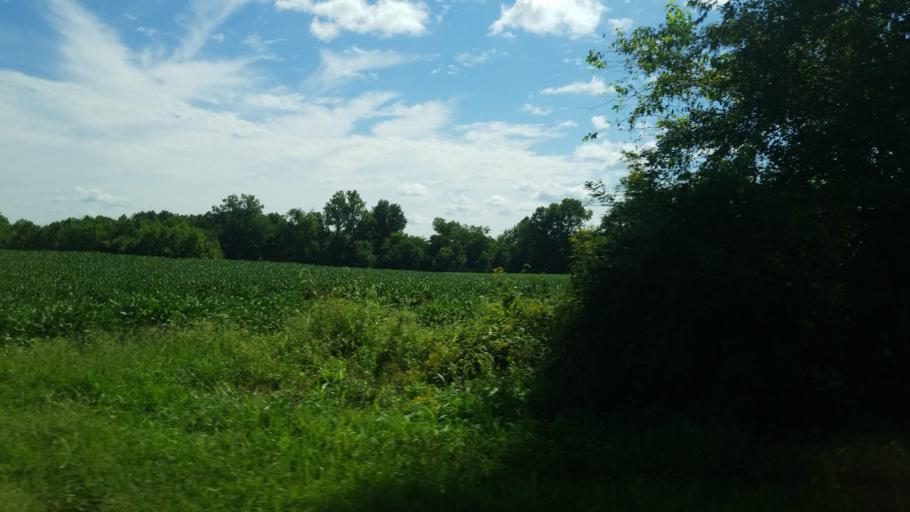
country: US
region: Illinois
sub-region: Williamson County
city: Johnston City
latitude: 37.7892
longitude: -88.9211
